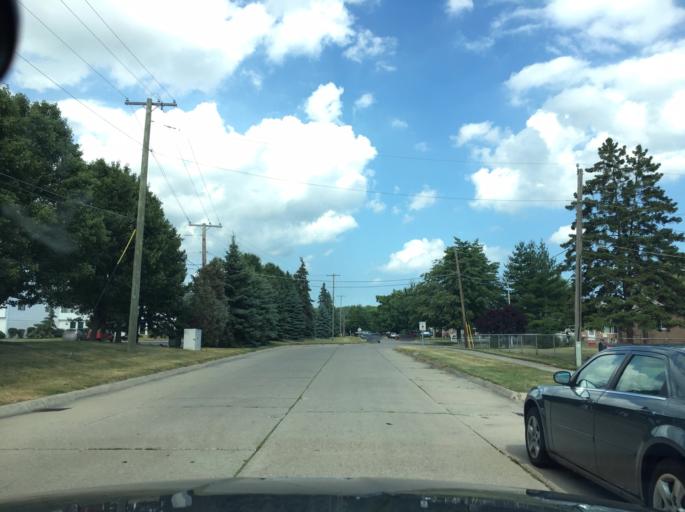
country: US
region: Michigan
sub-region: Macomb County
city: Fraser
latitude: 42.5467
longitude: -82.9253
